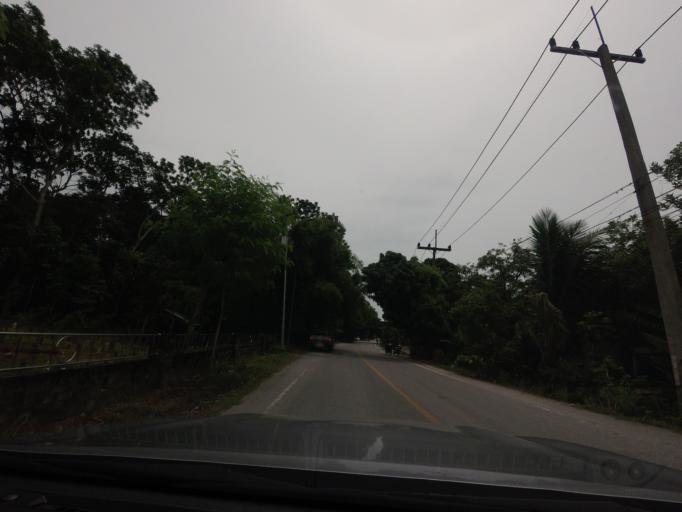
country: TH
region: Pattani
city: Sai Buri
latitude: 6.6449
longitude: 101.5515
